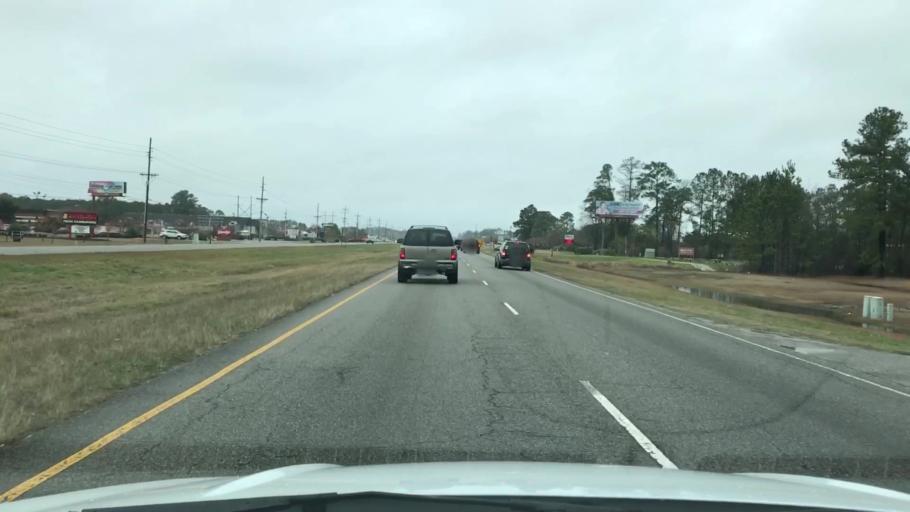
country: US
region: South Carolina
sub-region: Horry County
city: Red Hill
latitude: 33.7864
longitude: -78.9929
